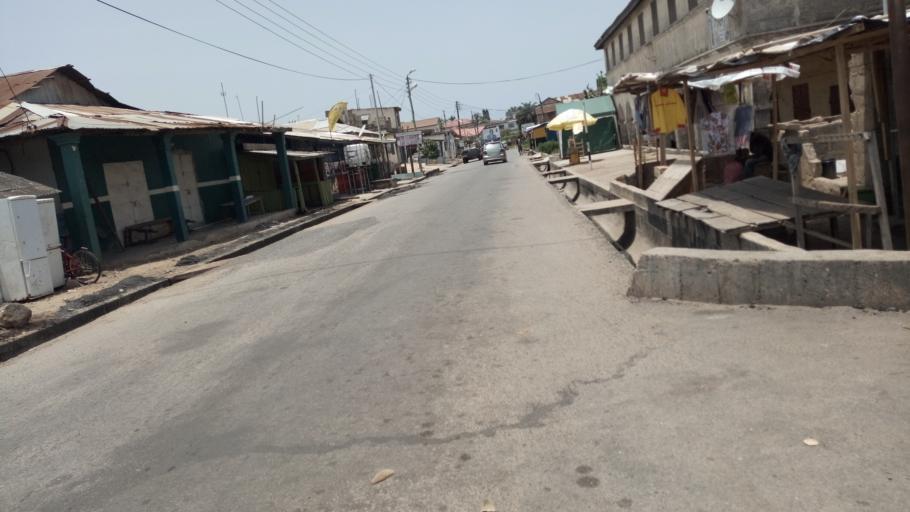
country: GH
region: Central
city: Winneba
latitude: 5.3471
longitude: -0.6266
